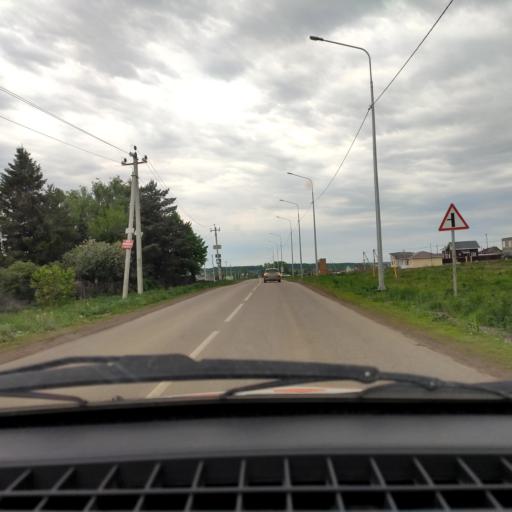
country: RU
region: Bashkortostan
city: Avdon
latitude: 54.5561
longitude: 55.7613
